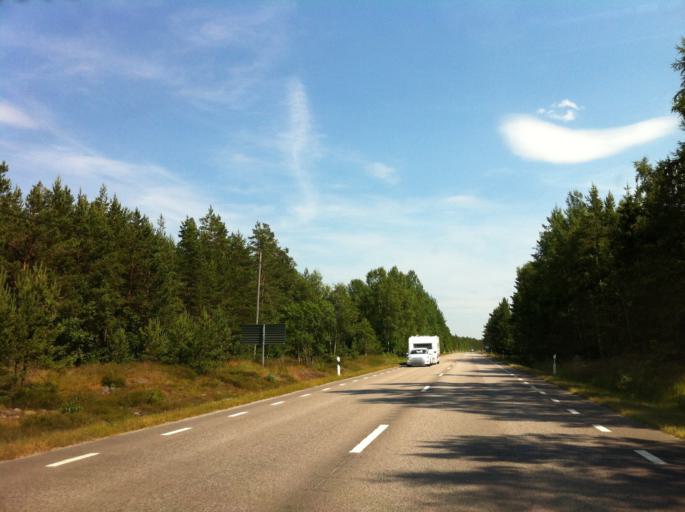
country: SE
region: Kalmar
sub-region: Nybro Kommun
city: Nybro
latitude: 56.8399
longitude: 15.7189
